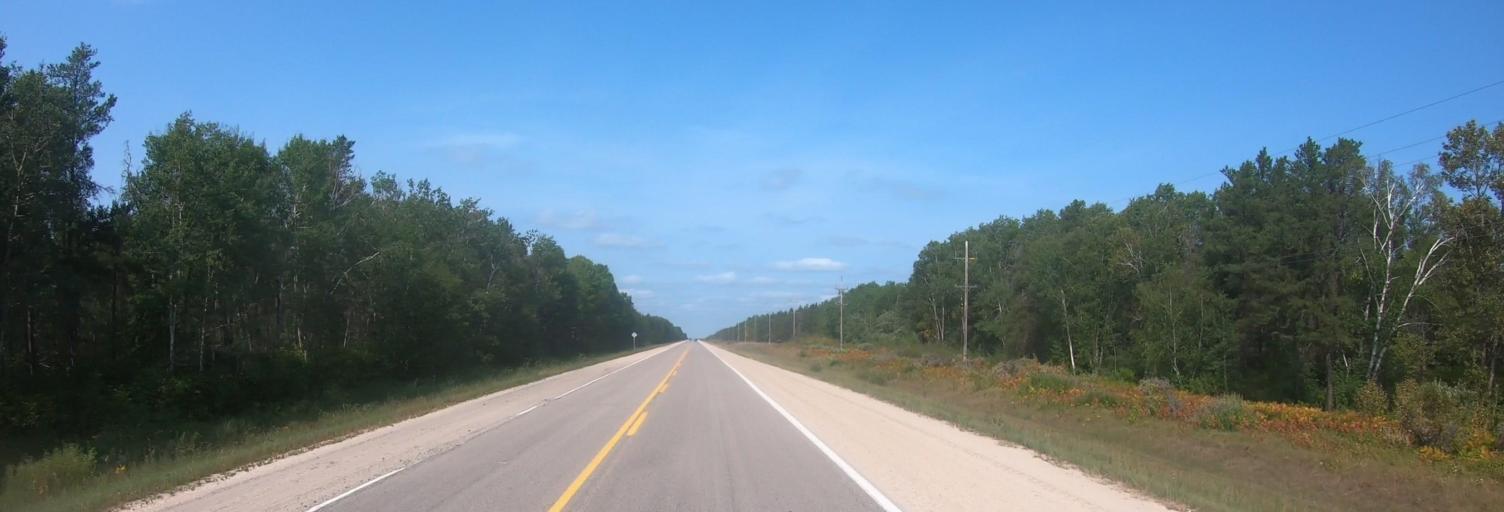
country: CA
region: Manitoba
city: La Broquerie
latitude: 49.1749
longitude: -96.1653
